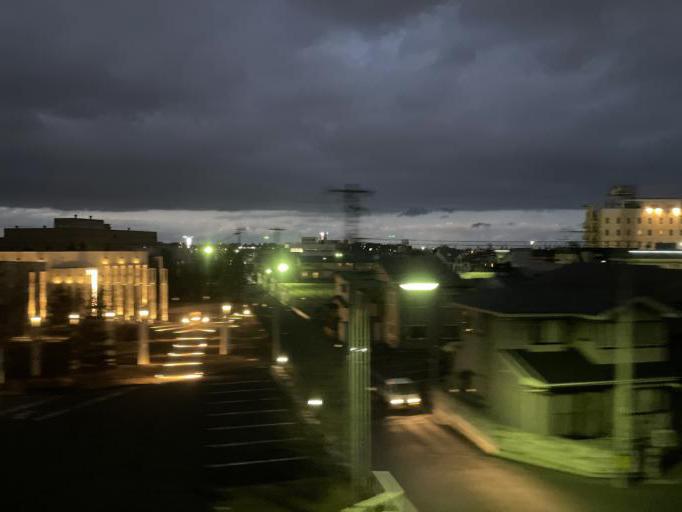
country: JP
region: Aomori
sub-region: Hachinohe Shi
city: Uchimaru
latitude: 40.5166
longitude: 141.4857
